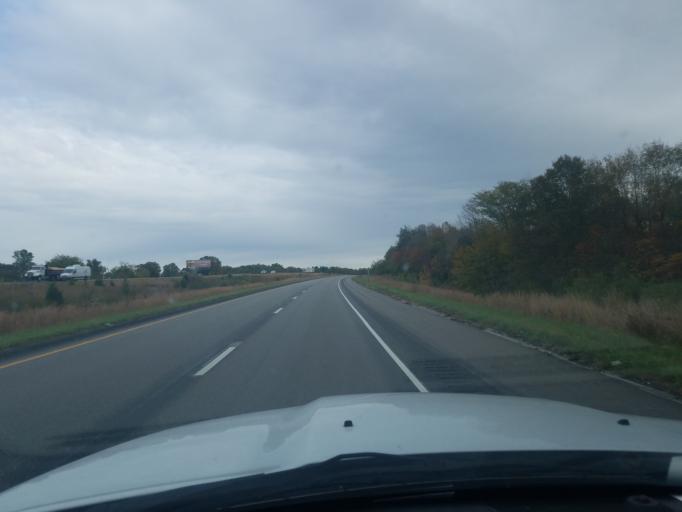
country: US
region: Indiana
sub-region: Spencer County
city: Dale
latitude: 38.2004
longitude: -87.1113
